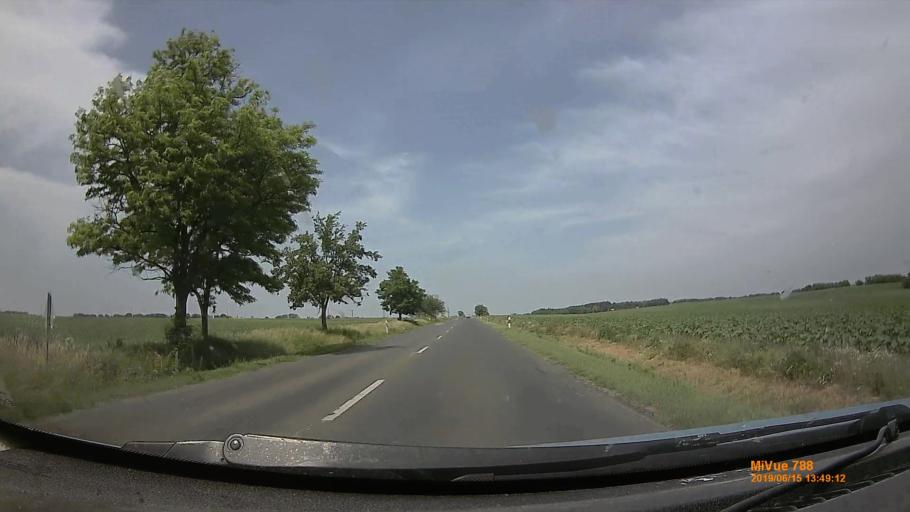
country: HU
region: Tolna
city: Iregszemcse
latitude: 46.7261
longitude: 18.1697
